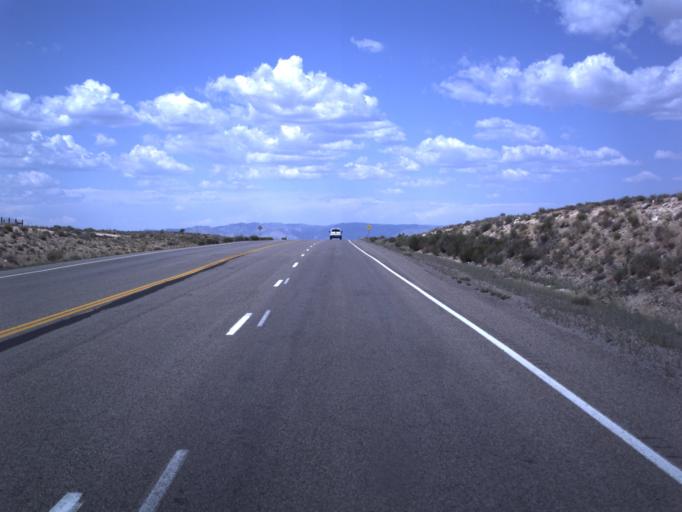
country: US
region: Utah
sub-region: Carbon County
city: Price
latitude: 39.4767
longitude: -110.8540
